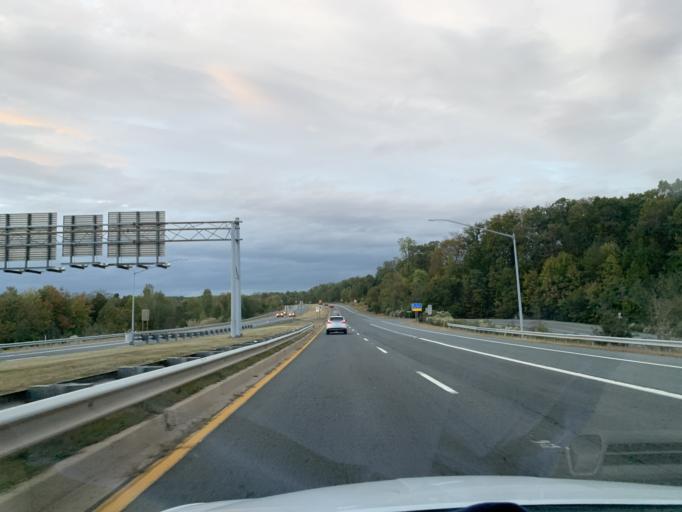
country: US
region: Maryland
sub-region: Harford County
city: Riverside
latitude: 39.4857
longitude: -76.2524
